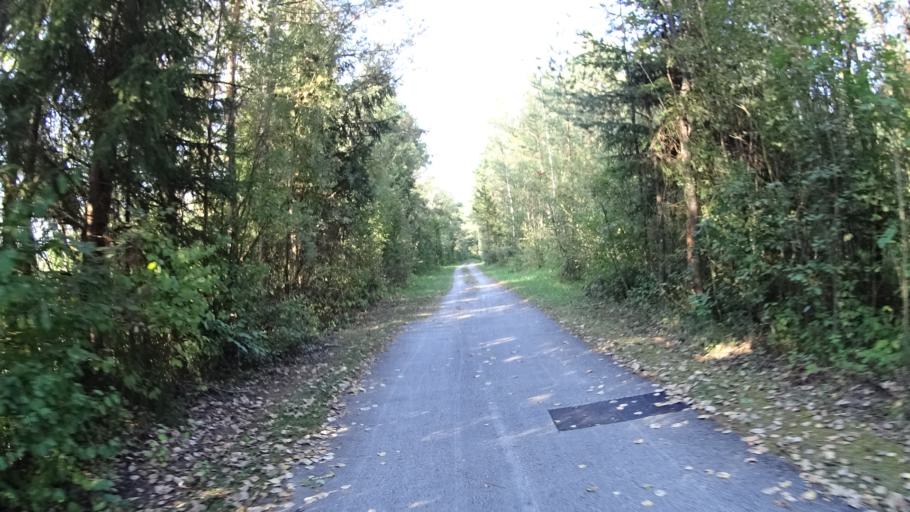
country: AT
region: Carinthia
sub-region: Politischer Bezirk Villach Land
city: Rosegg
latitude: 46.5720
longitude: 14.0389
